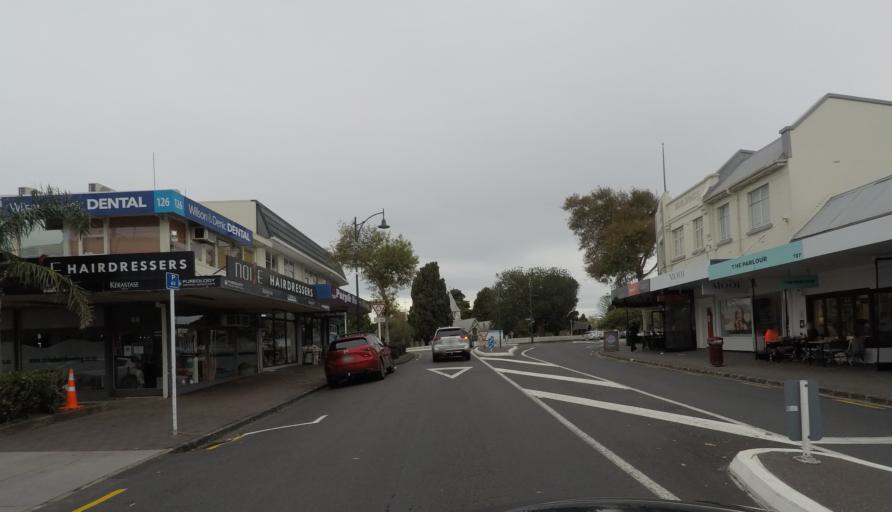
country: NZ
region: Auckland
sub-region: Auckland
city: Pakuranga
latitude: -36.8950
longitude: 174.9331
